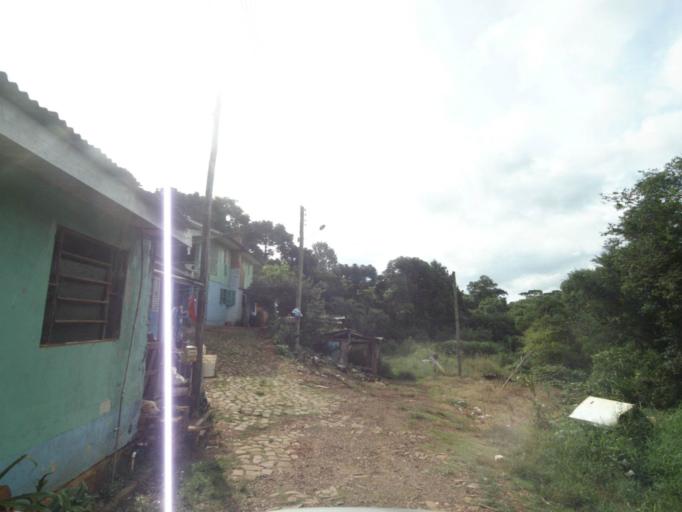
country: BR
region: Rio Grande do Sul
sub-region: Lagoa Vermelha
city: Lagoa Vermelha
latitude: -28.2065
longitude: -51.5336
